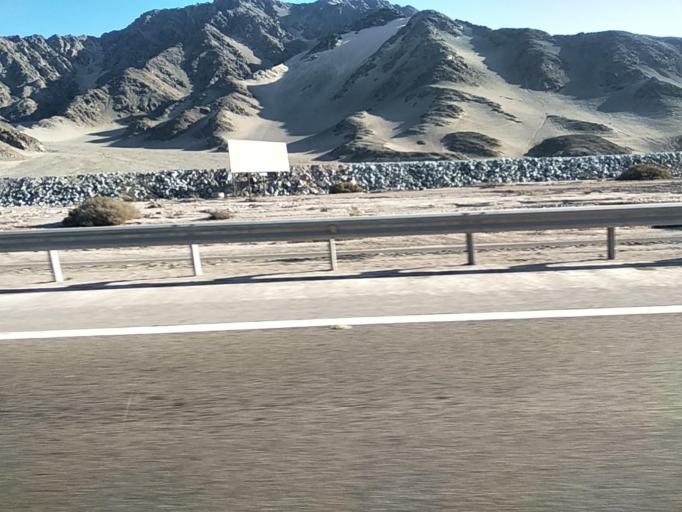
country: CL
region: Atacama
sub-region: Provincia de Copiapo
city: Copiapo
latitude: -27.3109
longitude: -70.4147
